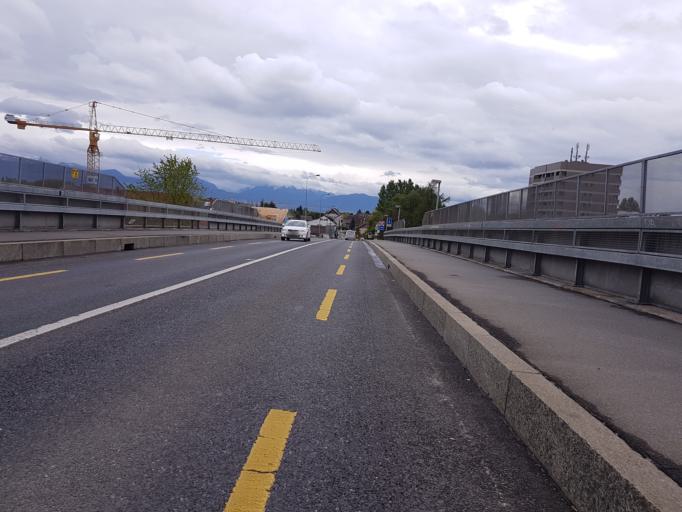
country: CH
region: Vaud
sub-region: Morges District
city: Preverenges
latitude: 46.5289
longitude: 6.5417
